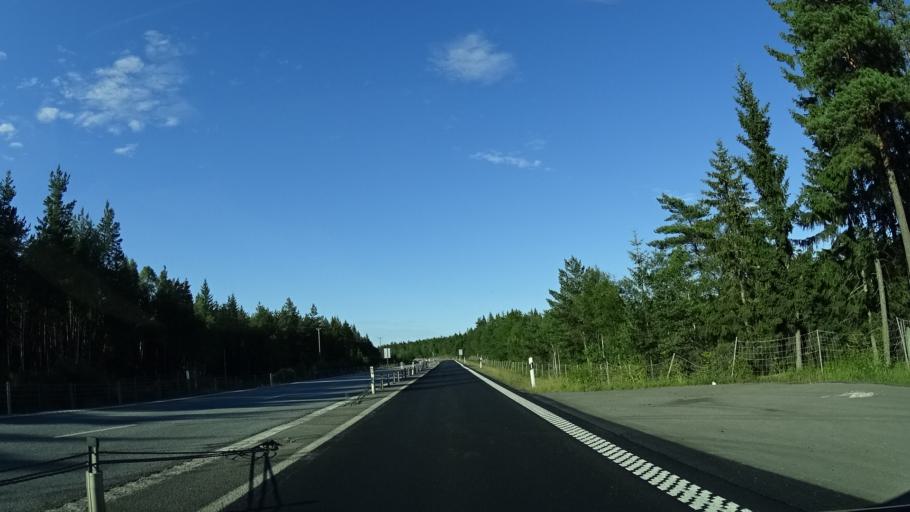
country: SE
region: Stockholm
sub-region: Osterakers Kommun
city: Akersberga
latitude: 59.5887
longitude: 18.2593
